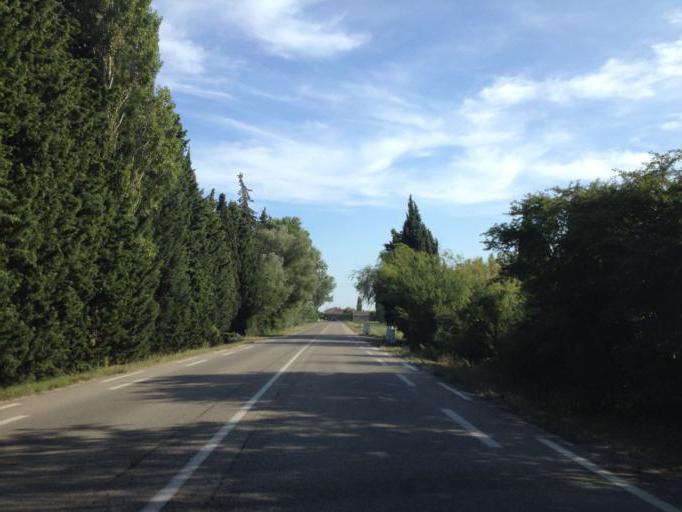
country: FR
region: Provence-Alpes-Cote d'Azur
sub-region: Departement du Vaucluse
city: Orange
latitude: 44.1326
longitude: 4.7838
